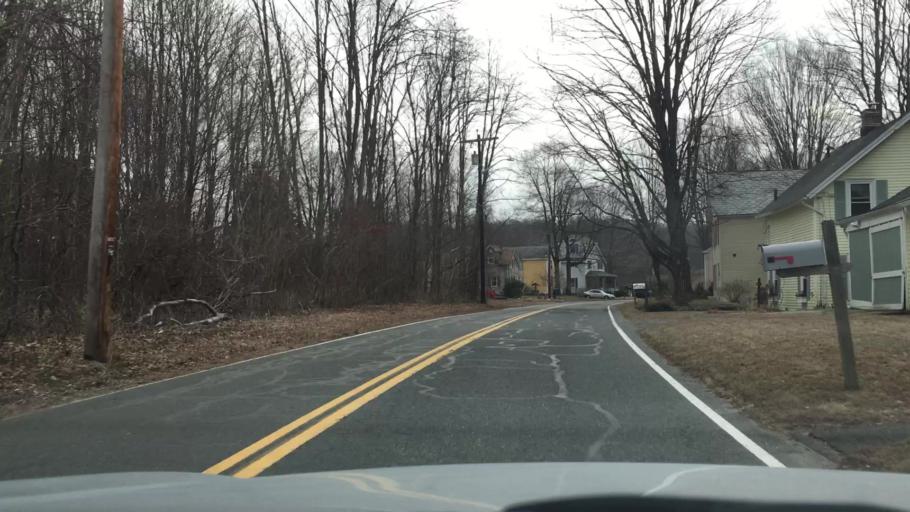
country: US
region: Massachusetts
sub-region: Hampshire County
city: Northampton
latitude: 42.3298
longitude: -72.6722
